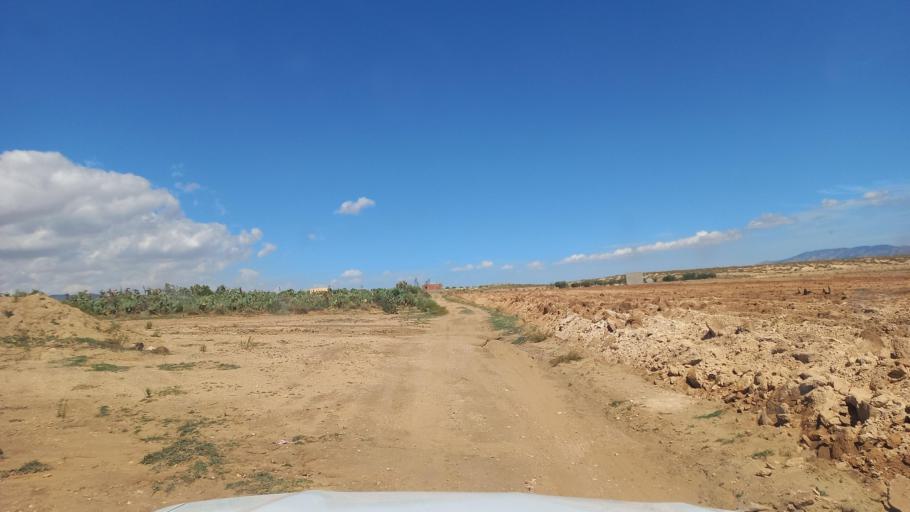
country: TN
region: Al Qasrayn
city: Sbiba
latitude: 35.3474
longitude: 9.0147
